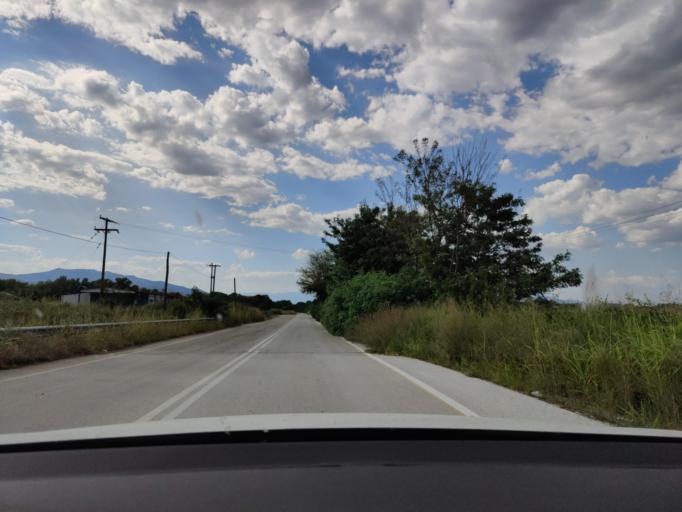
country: GR
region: Central Macedonia
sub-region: Nomos Serron
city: Strymoniko
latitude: 41.0520
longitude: 23.3220
